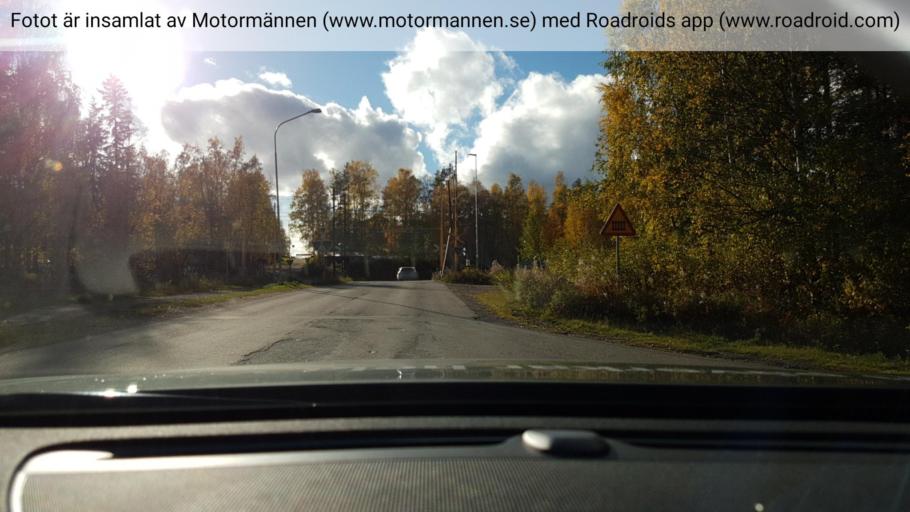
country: SE
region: Norrbotten
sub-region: Gallivare Kommun
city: Malmberget
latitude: 67.1850
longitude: 20.7356
